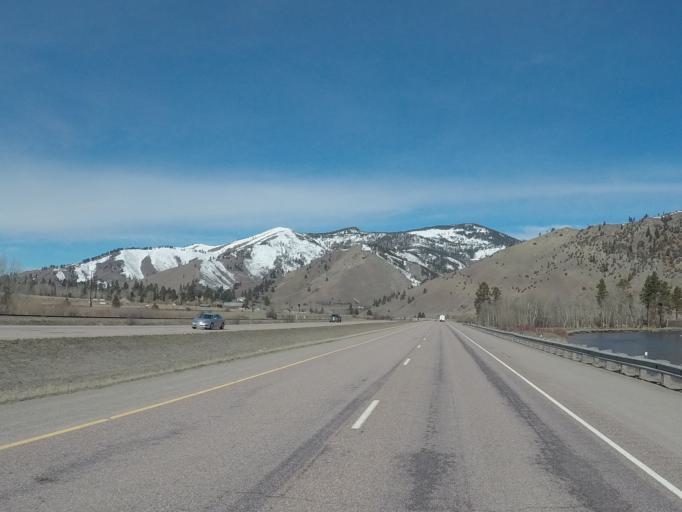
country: US
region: Montana
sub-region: Missoula County
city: Clinton
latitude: 46.6995
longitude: -113.3617
